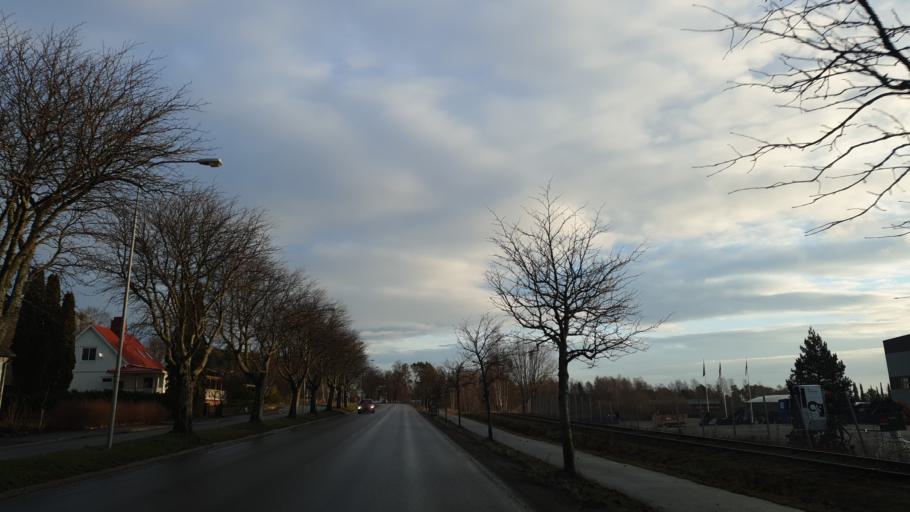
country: SE
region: Gaevleborg
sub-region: Hudiksvalls Kommun
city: Hudiksvall
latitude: 61.7244
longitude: 17.1367
